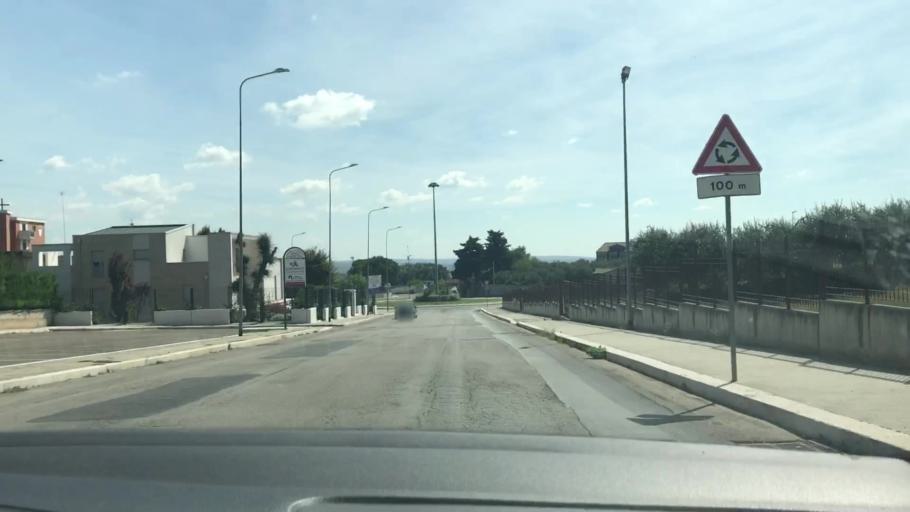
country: IT
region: Apulia
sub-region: Provincia di Bari
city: Altamura
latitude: 40.8258
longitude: 16.5651
